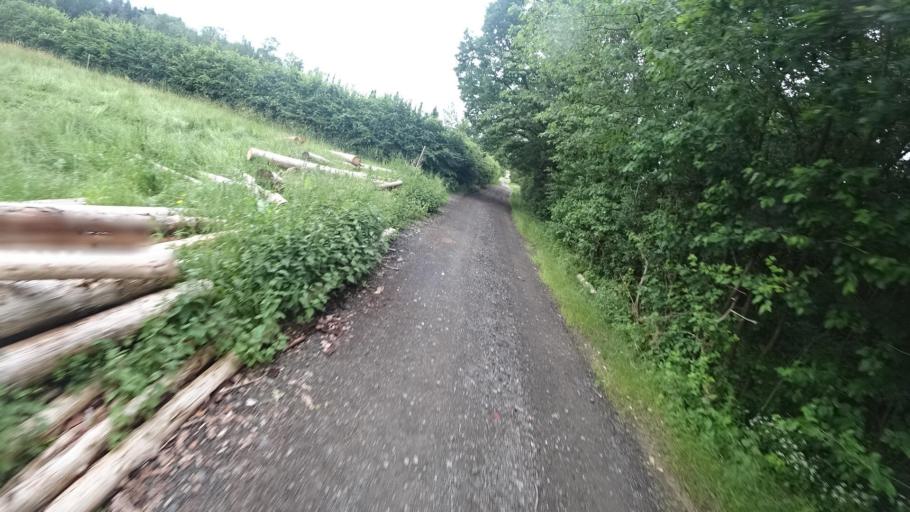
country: DE
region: Rheinland-Pfalz
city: Mayschoss
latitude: 50.5408
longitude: 7.0318
